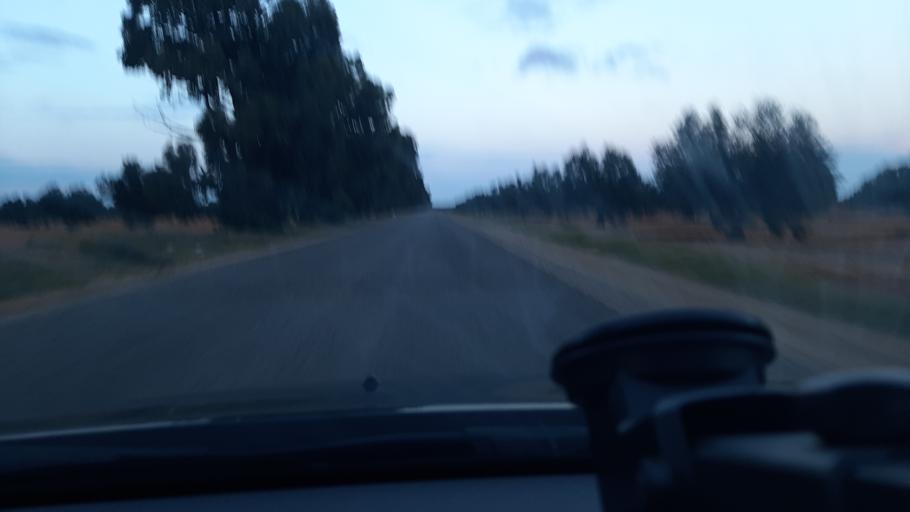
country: TN
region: Al Mahdiyah
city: Shurban
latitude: 34.9762
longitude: 10.3786
